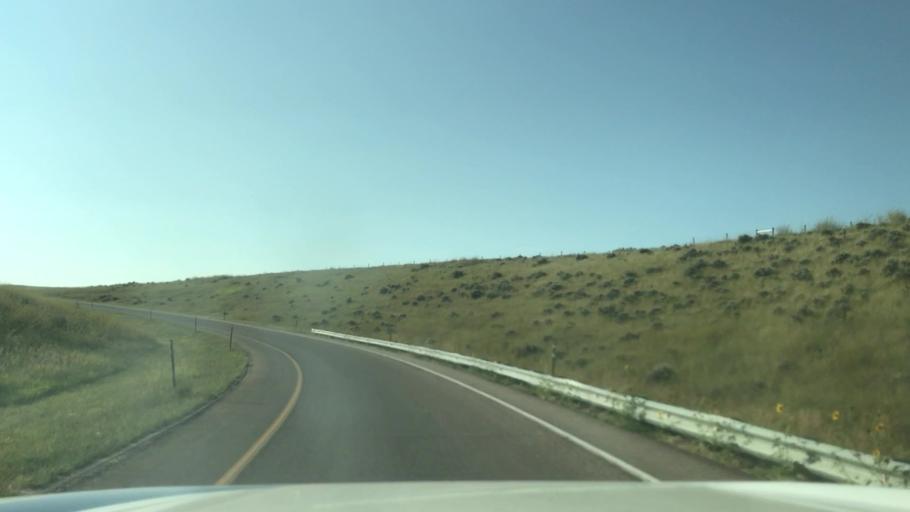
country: US
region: Wyoming
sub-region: Converse County
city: Douglas
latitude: 42.7300
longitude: -105.3407
